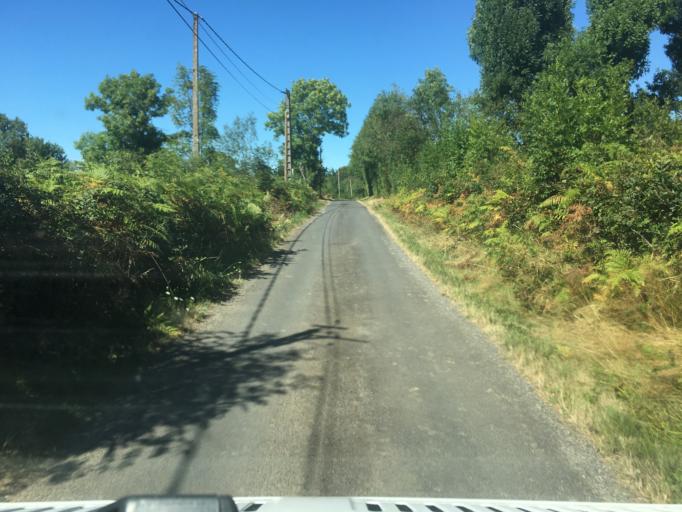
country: FR
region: Limousin
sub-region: Departement de la Correze
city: Bort-les-Orgues
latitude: 45.4408
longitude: 2.4866
